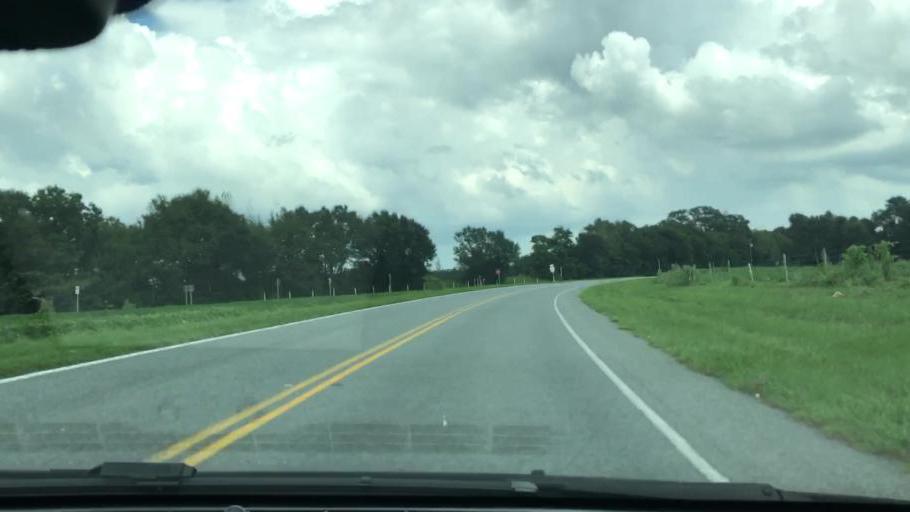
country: US
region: Florida
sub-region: Jackson County
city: Malone
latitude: 30.9605
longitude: -85.1179
